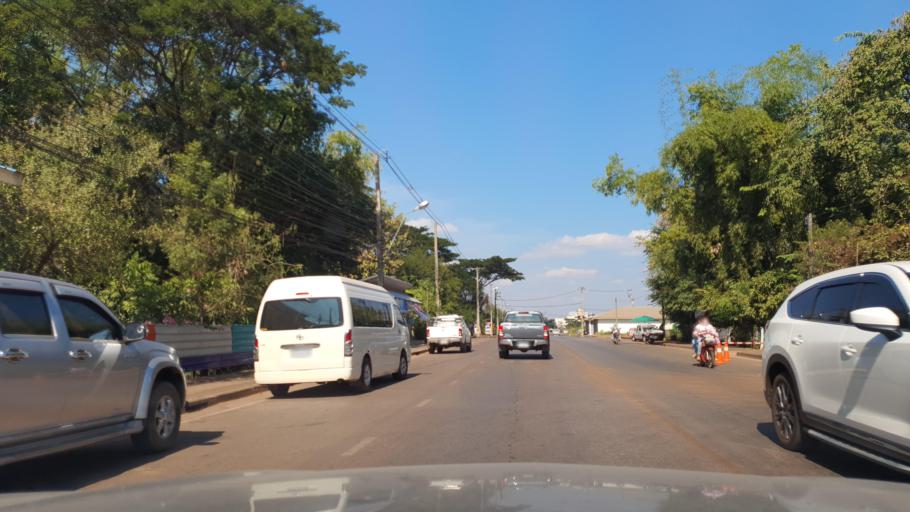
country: TH
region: Sakon Nakhon
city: Sakon Nakhon
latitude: 17.1686
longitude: 104.1250
